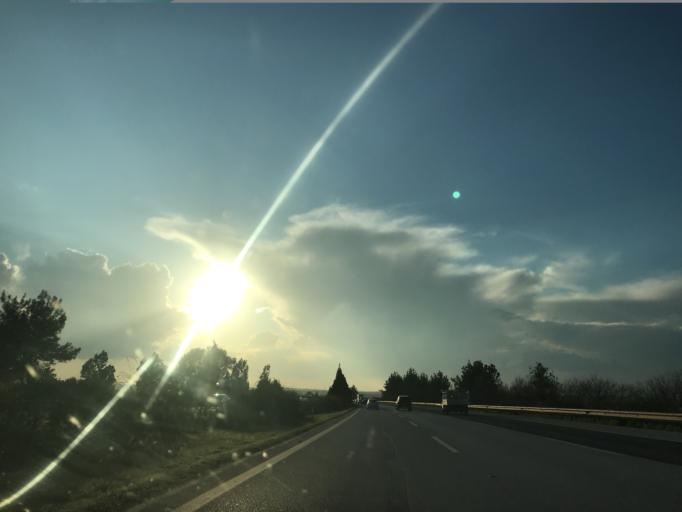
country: TR
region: Adana
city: Yakapinar
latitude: 37.0076
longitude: 35.6804
